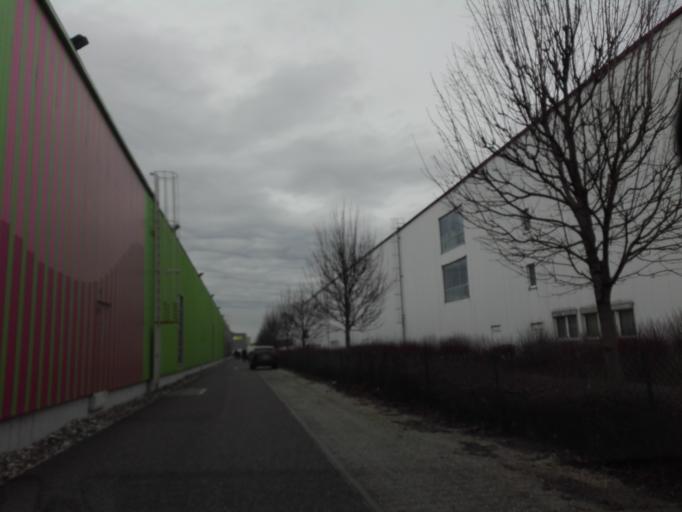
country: AT
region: Upper Austria
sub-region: Politischer Bezirk Linz-Land
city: Ansfelden
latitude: 48.2158
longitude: 14.2856
